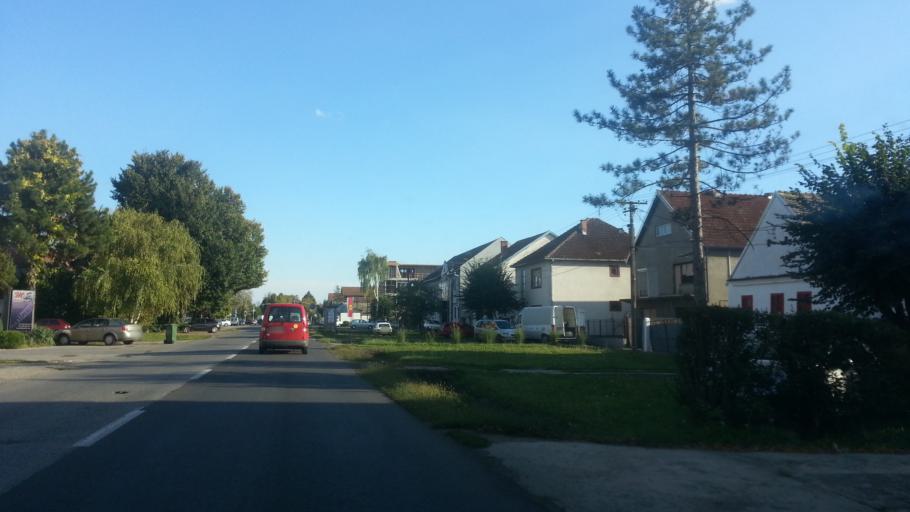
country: RS
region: Autonomna Pokrajina Vojvodina
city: Nova Pazova
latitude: 44.9413
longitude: 20.2237
